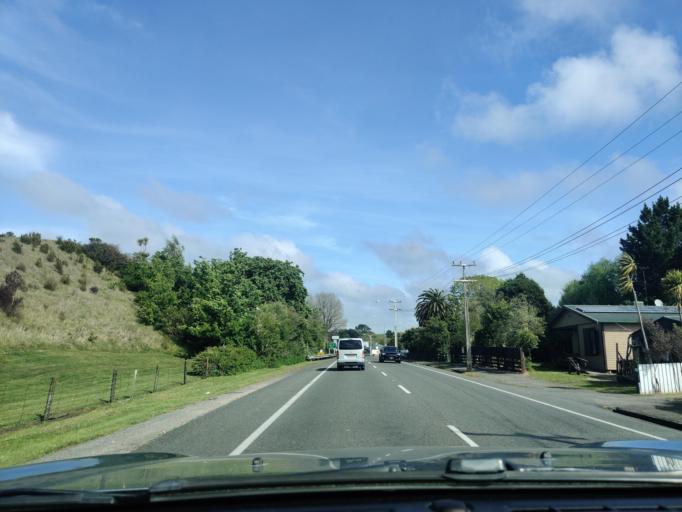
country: NZ
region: Manawatu-Wanganui
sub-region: Wanganui District
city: Wanganui
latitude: -40.0446
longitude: 175.2126
